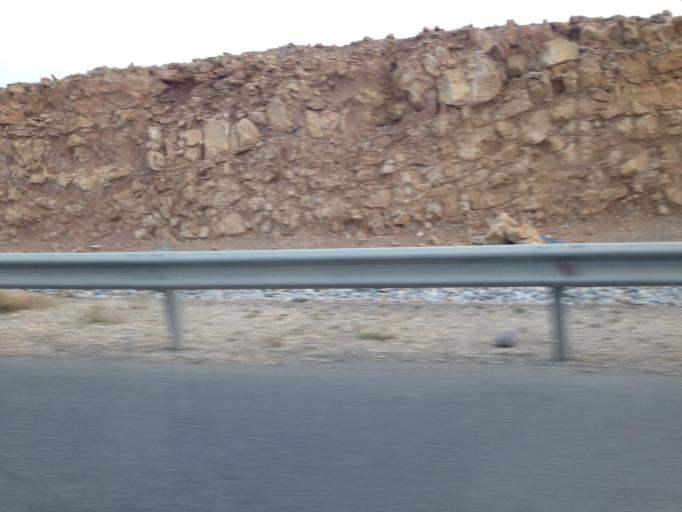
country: OM
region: Muhafazat Masqat
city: Bawshar
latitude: 23.5591
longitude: 58.3377
